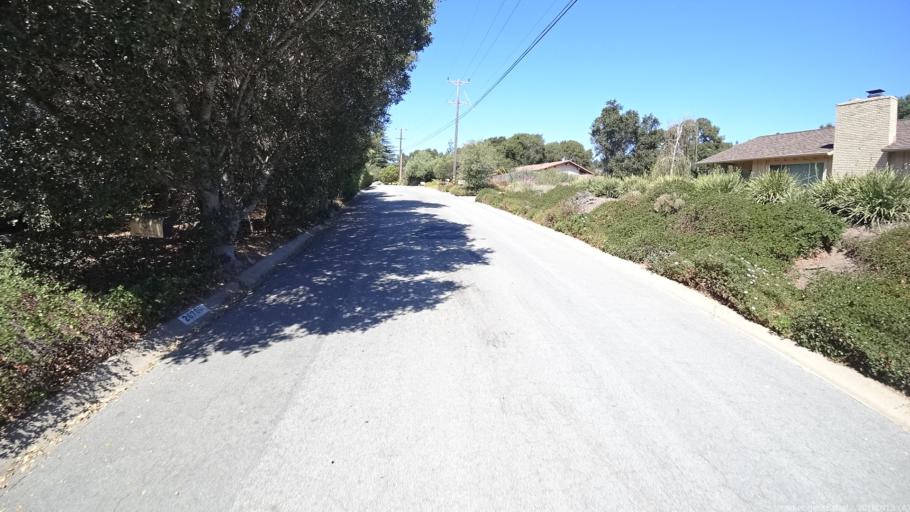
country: US
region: California
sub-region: Monterey County
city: Del Rey Oaks
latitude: 36.5362
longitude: -121.8598
